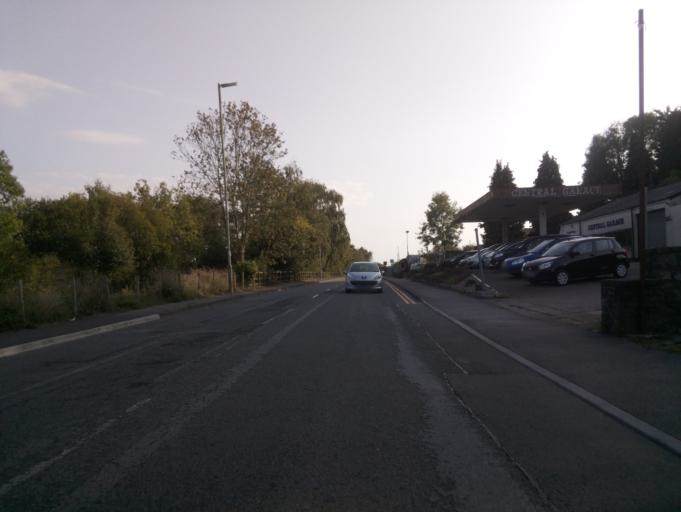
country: GB
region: Wales
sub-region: Torfaen County Borough
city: New Inn
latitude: 51.6795
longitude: -3.0204
